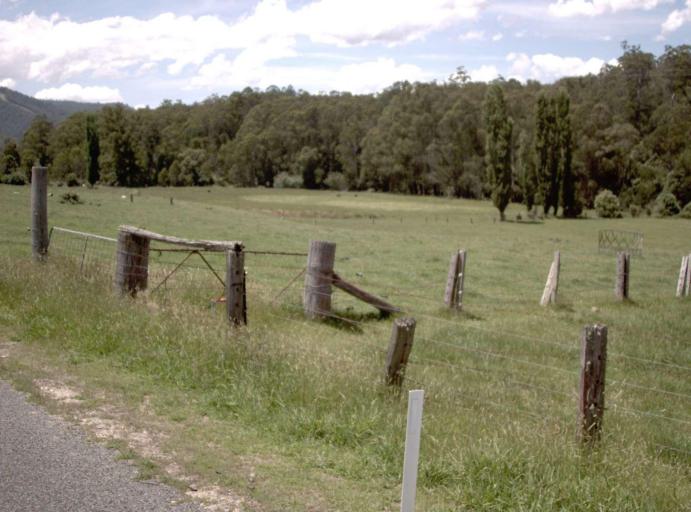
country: AU
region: New South Wales
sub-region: Bombala
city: Bombala
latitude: -37.3814
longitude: 149.0133
